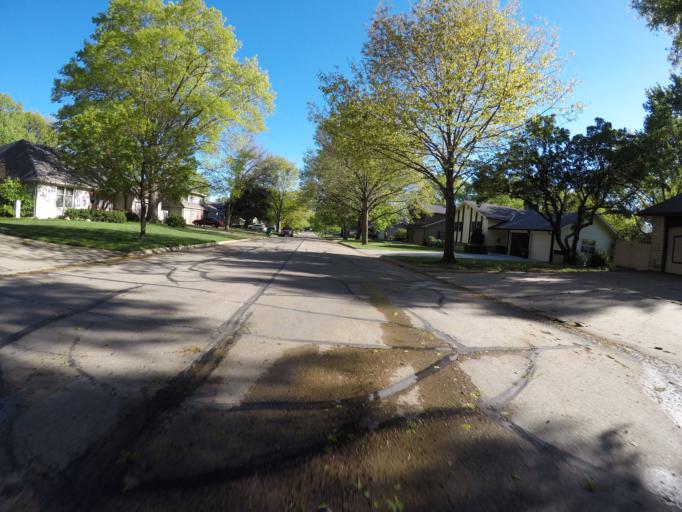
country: US
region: Kansas
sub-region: Riley County
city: Manhattan
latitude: 39.2019
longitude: -96.6116
